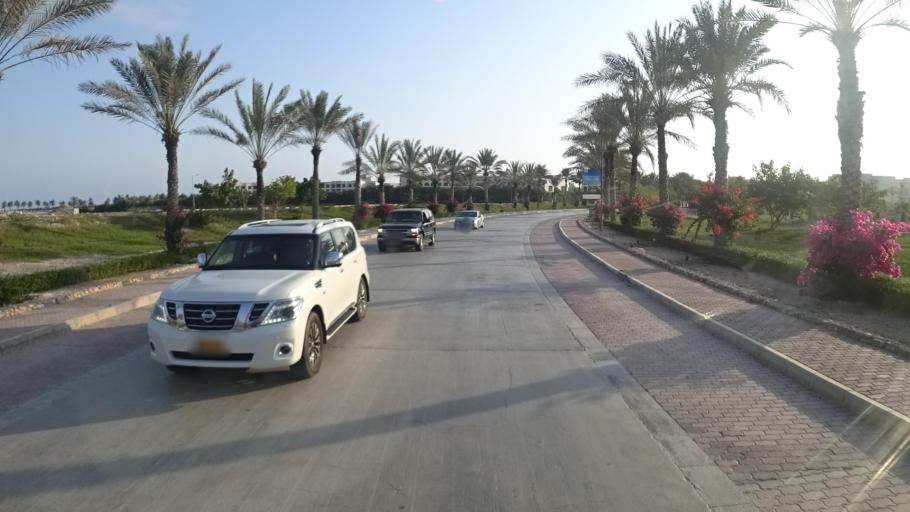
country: OM
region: Zufar
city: Salalah
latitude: 17.0360
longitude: 54.3033
